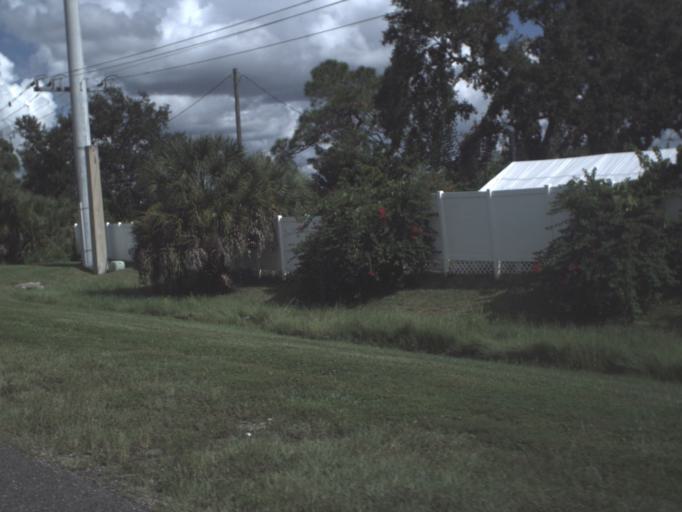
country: US
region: Florida
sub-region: Sarasota County
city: Warm Mineral Springs
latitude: 27.0475
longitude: -82.2887
